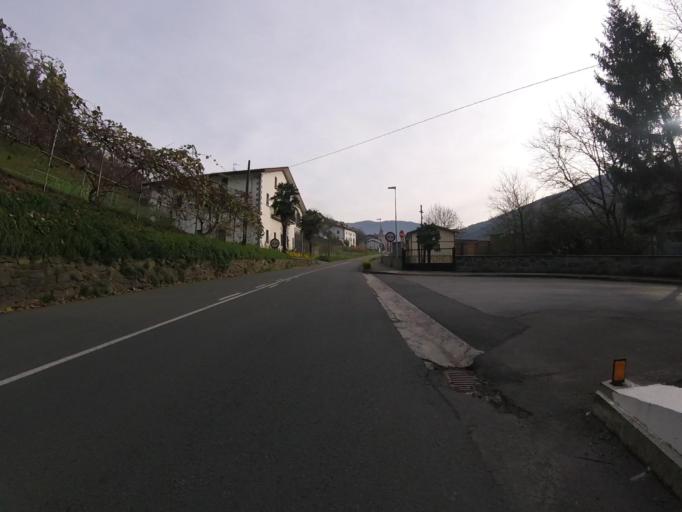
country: ES
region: Basque Country
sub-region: Provincia de Guipuzcoa
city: Berrobi
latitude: 43.1460
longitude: -2.0302
